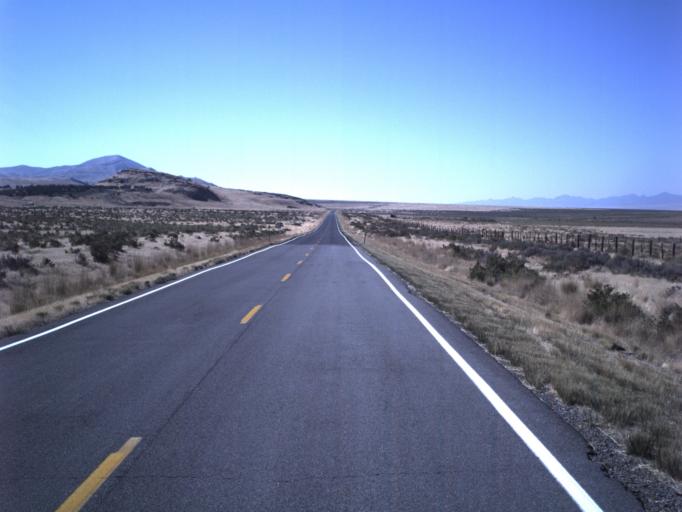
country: US
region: Utah
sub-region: Tooele County
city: Grantsville
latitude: 40.6241
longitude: -112.6987
